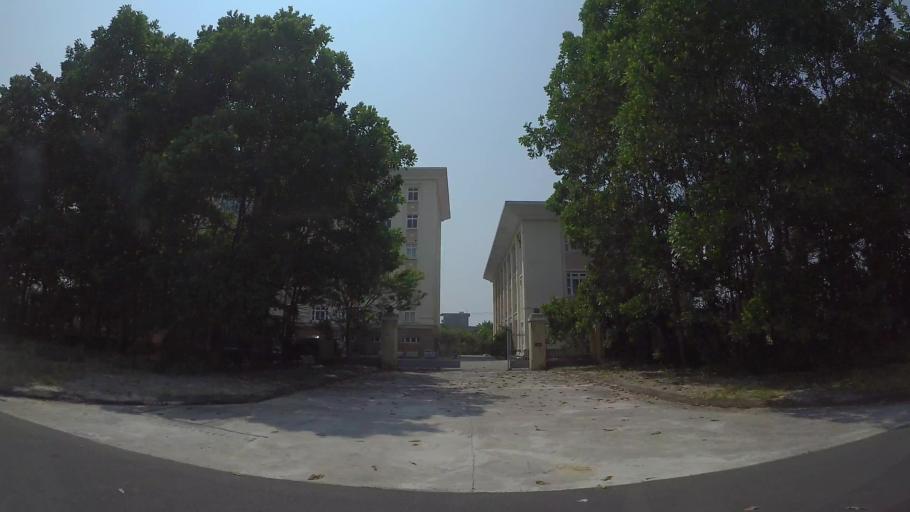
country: VN
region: Da Nang
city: Cam Le
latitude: 15.9822
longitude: 108.2114
